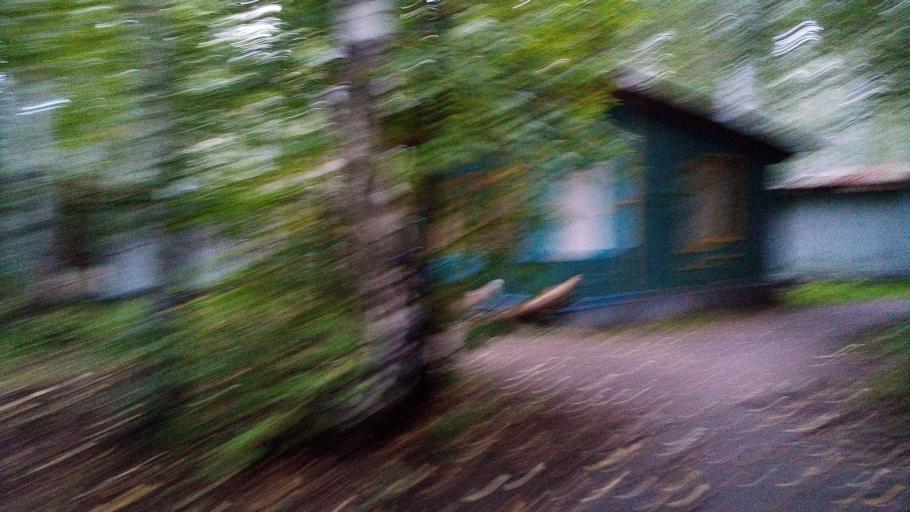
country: RU
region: Chelyabinsk
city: Tayginka
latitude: 55.4775
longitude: 60.4983
